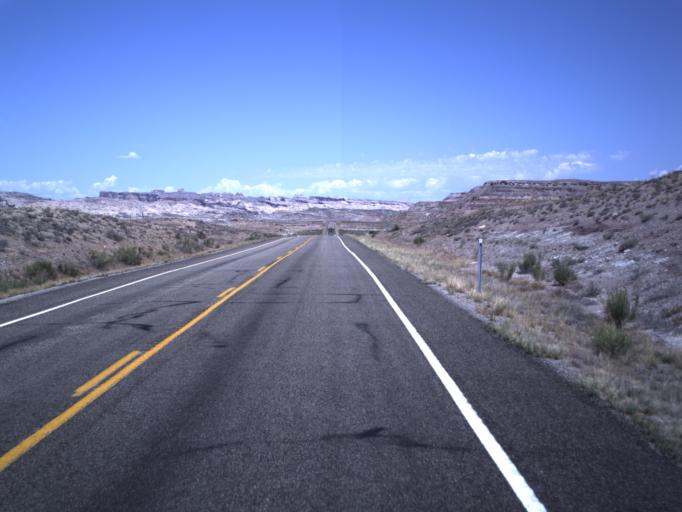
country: US
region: Utah
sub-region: Carbon County
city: East Carbon City
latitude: 38.8945
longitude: -110.3602
